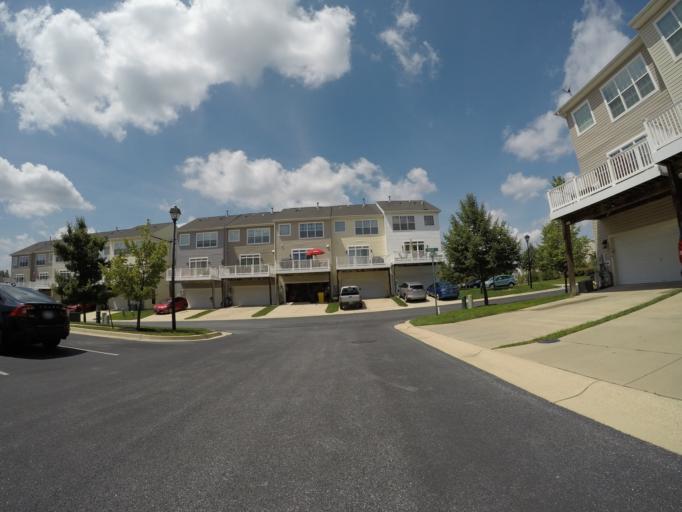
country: US
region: Maryland
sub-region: Anne Arundel County
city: Odenton
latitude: 39.0498
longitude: -76.7084
